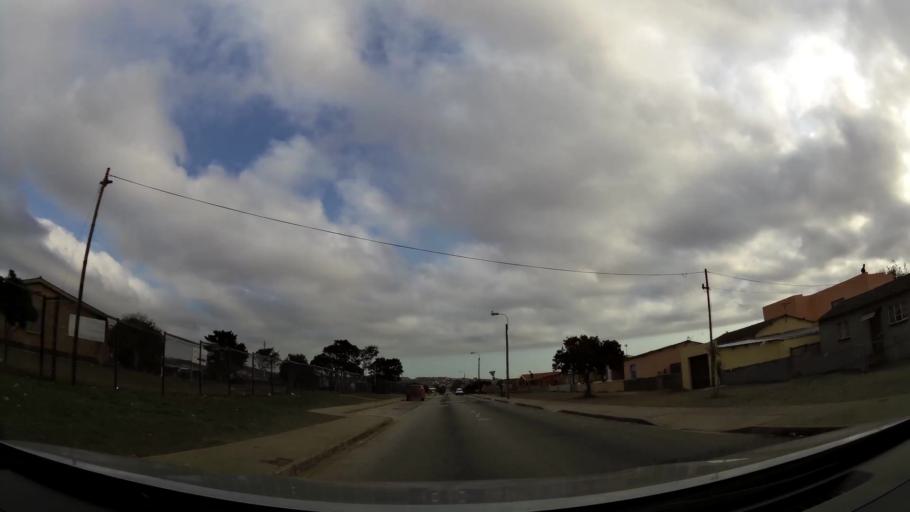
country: ZA
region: Eastern Cape
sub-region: Nelson Mandela Bay Metropolitan Municipality
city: Port Elizabeth
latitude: -33.9190
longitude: 25.5518
